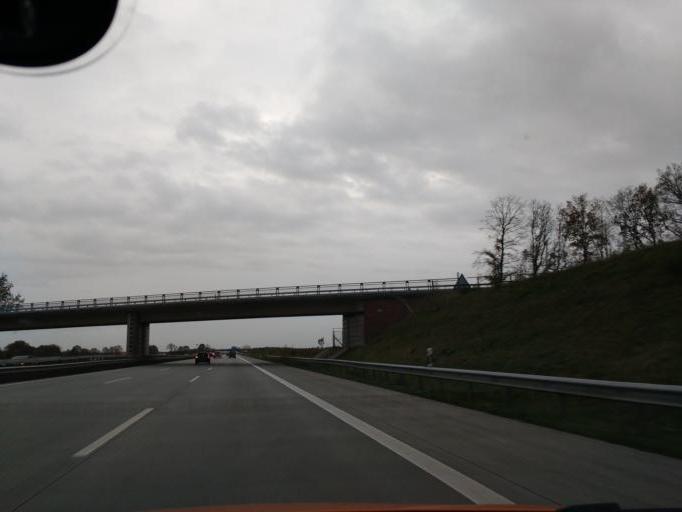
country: DE
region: Lower Saxony
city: Reessum
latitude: 53.1262
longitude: 9.2135
